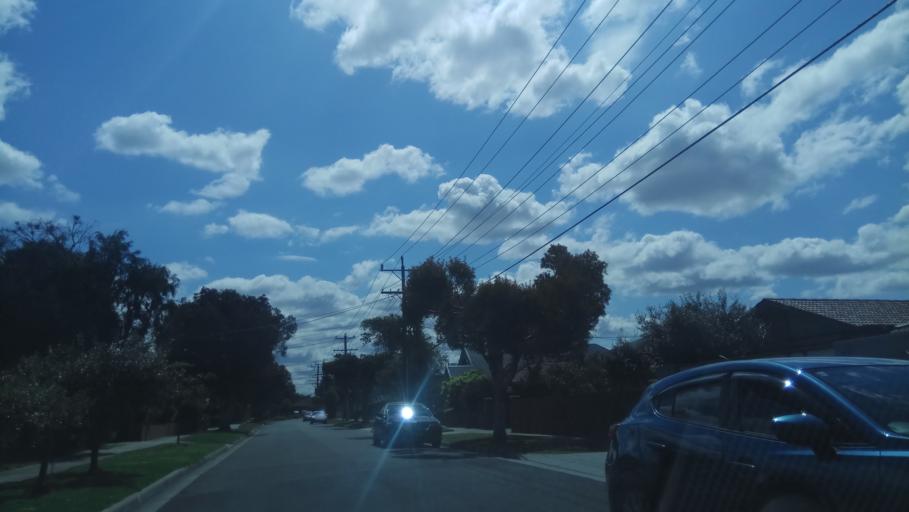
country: AU
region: Victoria
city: Heatherton
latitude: -37.9675
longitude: 145.0829
